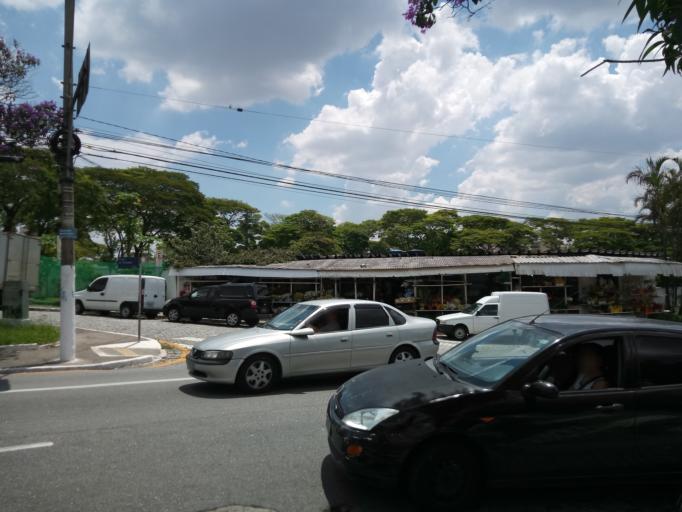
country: BR
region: Sao Paulo
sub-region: Sao Bernardo Do Campo
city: Sao Bernardo do Campo
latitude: -23.6936
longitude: -46.5577
